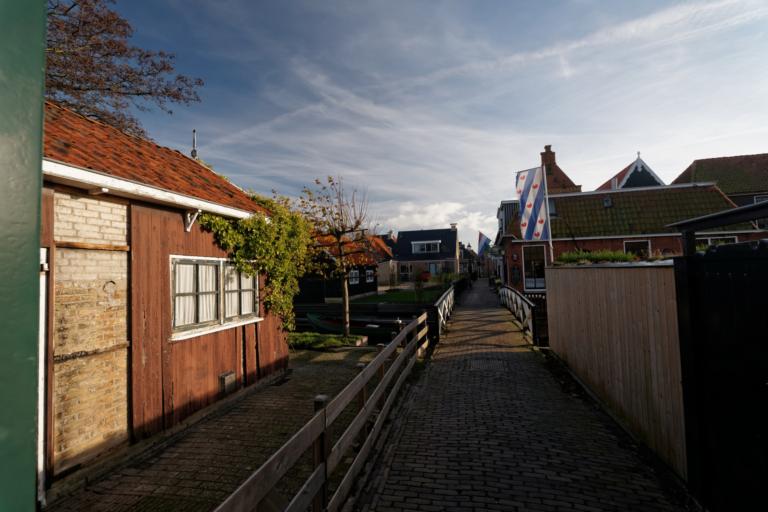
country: NL
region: Friesland
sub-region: Sudwest Fryslan
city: Koudum
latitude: 52.9420
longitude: 5.4006
